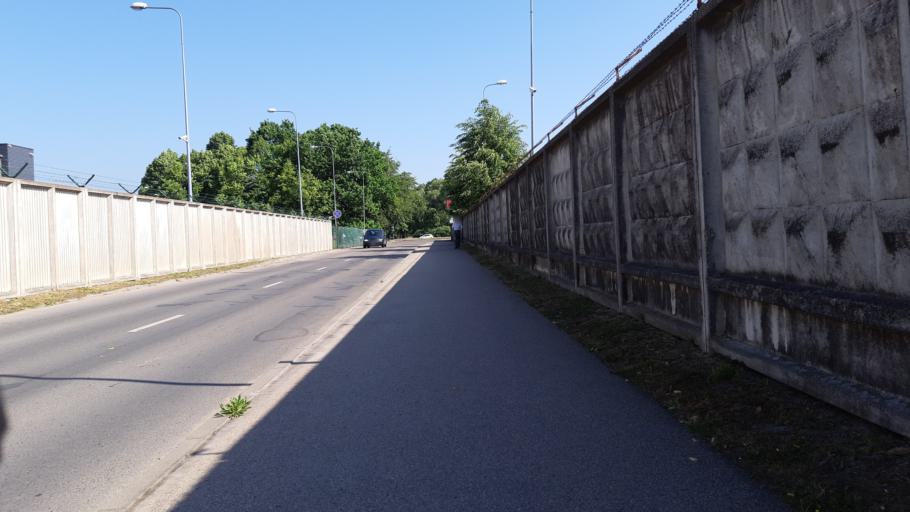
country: LT
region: Kauno apskritis
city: Dainava (Kaunas)
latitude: 54.9172
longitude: 23.9918
